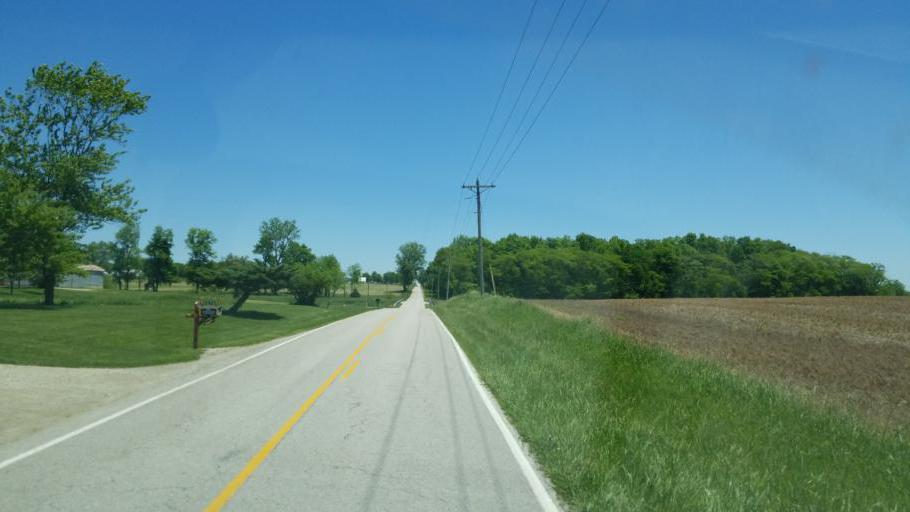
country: US
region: Ohio
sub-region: Darke County
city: Ansonia
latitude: 40.2647
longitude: -84.6310
